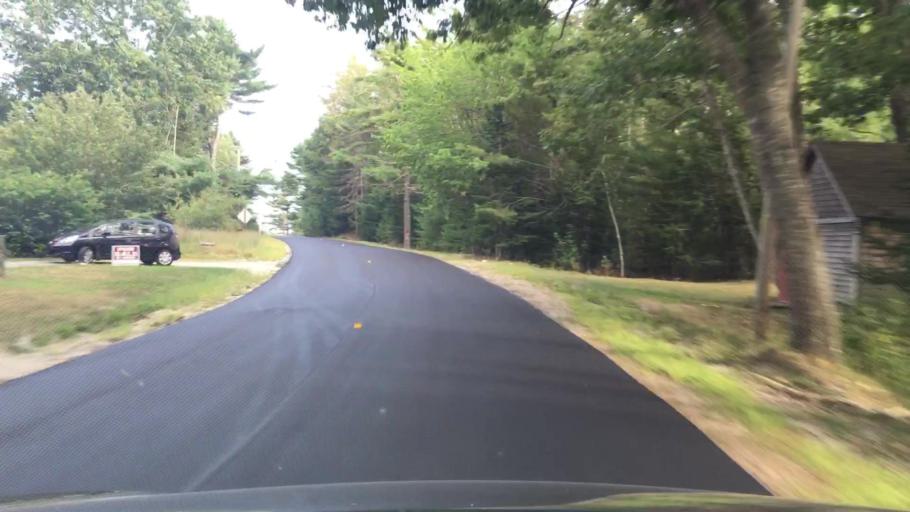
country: US
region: Maine
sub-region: Hancock County
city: Surry
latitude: 44.5173
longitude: -68.6064
